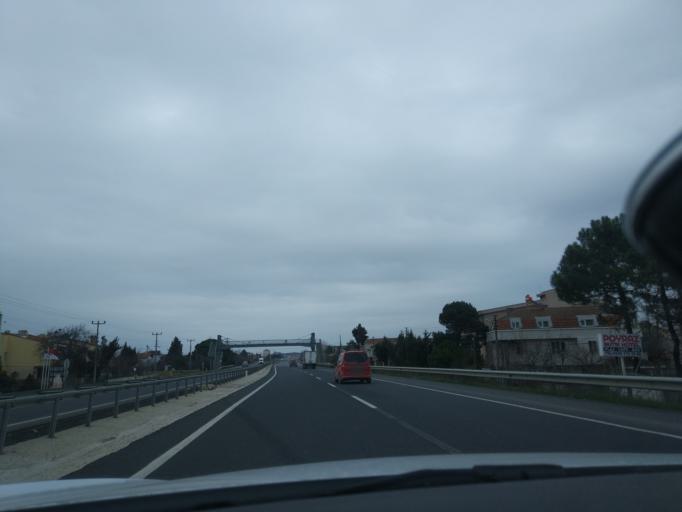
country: TR
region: Tekirdag
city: Marmara Ereglisi
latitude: 40.9712
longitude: 27.9230
